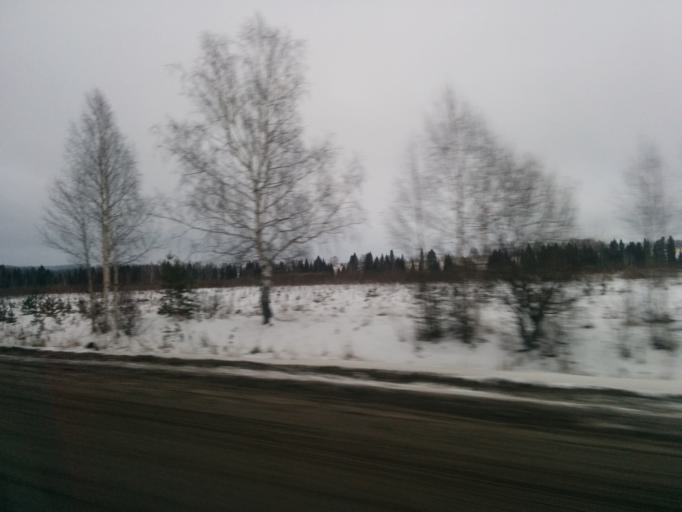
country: RU
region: Perm
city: Nytva
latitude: 57.9407
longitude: 55.1249
